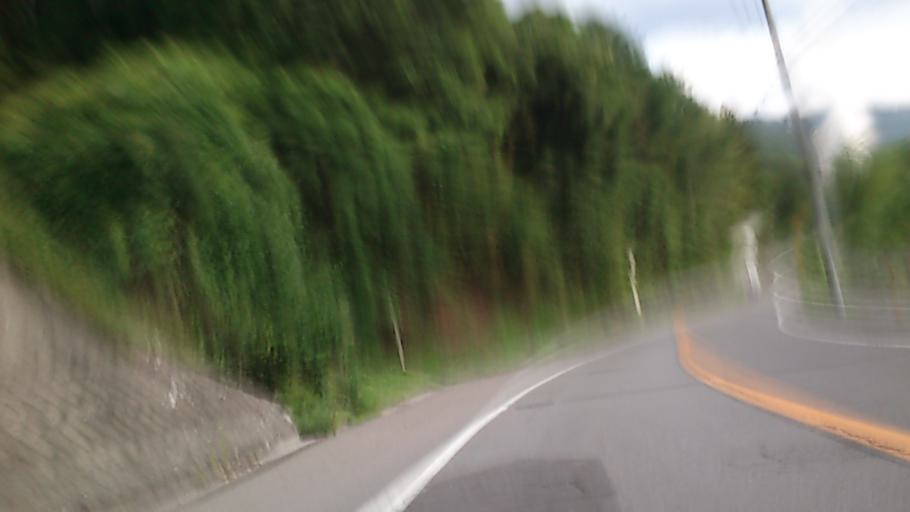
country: JP
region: Nagano
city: Suwa
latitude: 36.1136
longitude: 138.0990
